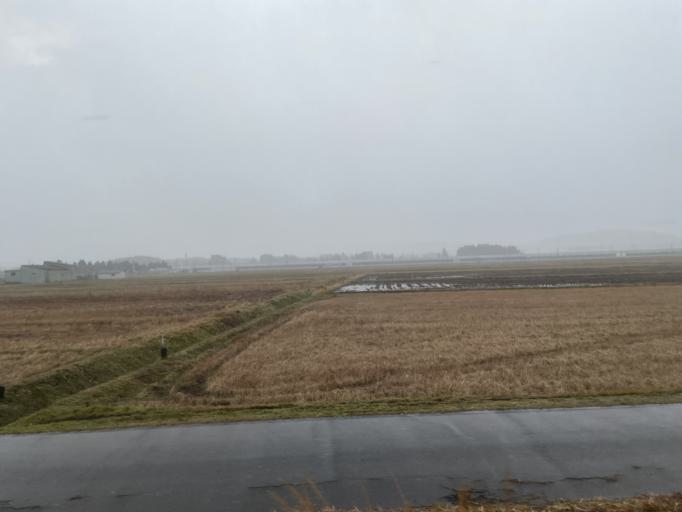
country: JP
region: Aomori
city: Aomori Shi
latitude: 40.8730
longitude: 140.6799
